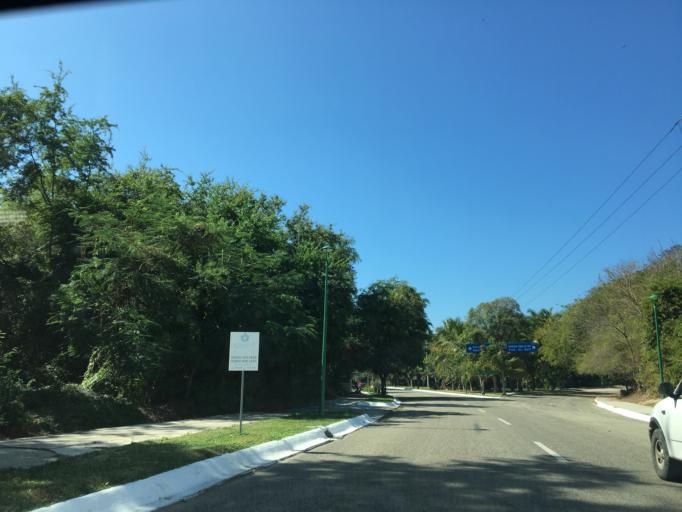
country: MX
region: Oaxaca
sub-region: Santa Maria Huatulco
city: Crucecita
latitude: 15.7758
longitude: -96.0983
